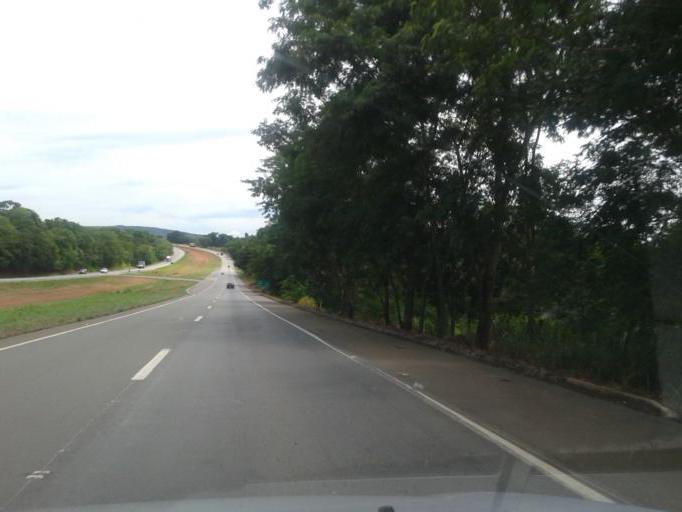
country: BR
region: Goias
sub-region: Hidrolandia
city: Hidrolandia
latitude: -17.1308
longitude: -49.2131
